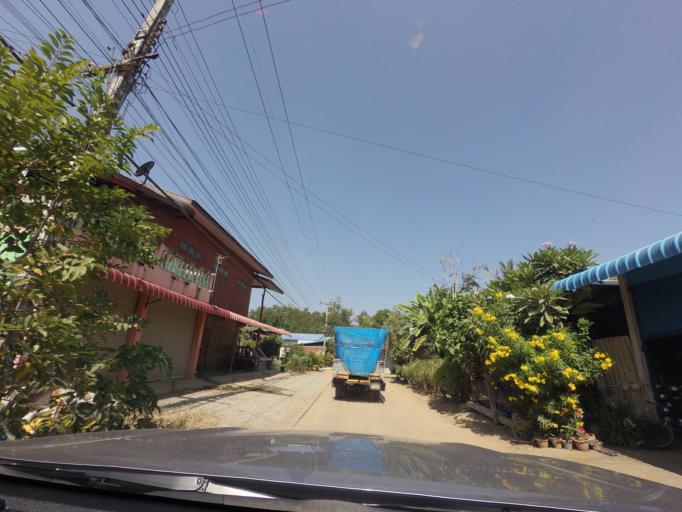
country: TH
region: Sukhothai
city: Si Samrong
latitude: 17.1992
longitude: 99.7726
